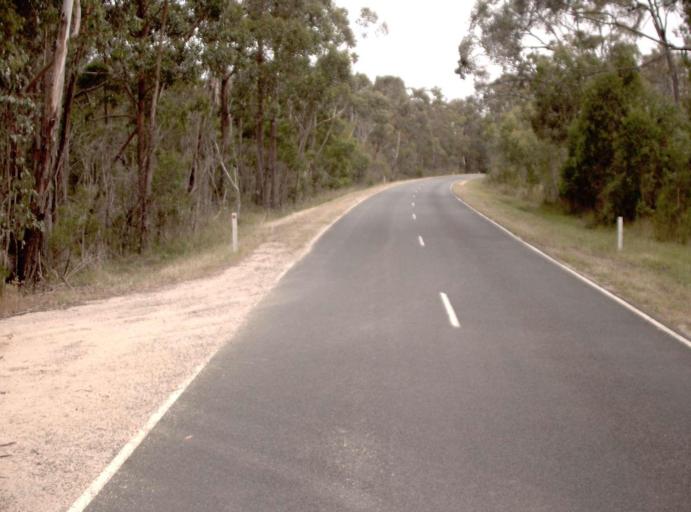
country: AU
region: Victoria
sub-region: Latrobe
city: Traralgon
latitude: -38.4421
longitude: 146.8242
